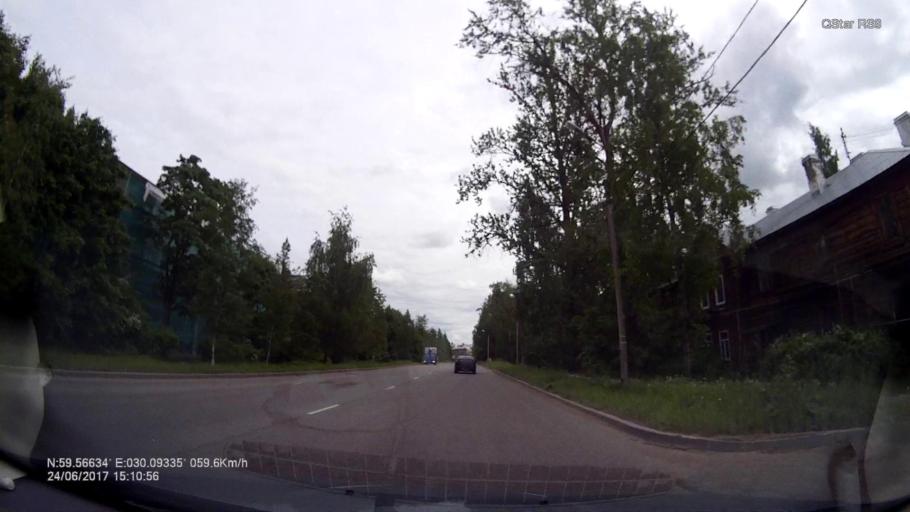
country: RU
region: Leningrad
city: Mariyenburg
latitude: 59.5662
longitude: 30.0936
